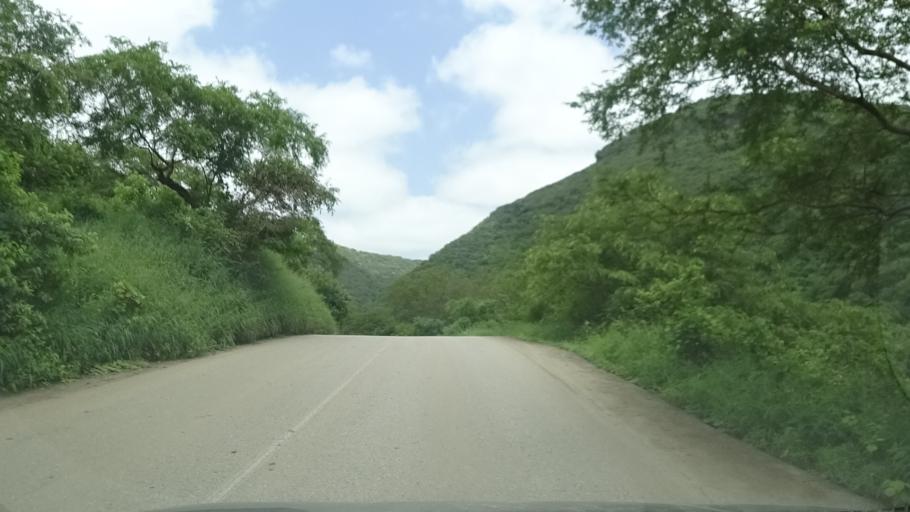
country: OM
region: Zufar
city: Salalah
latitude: 17.1562
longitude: 54.1726
